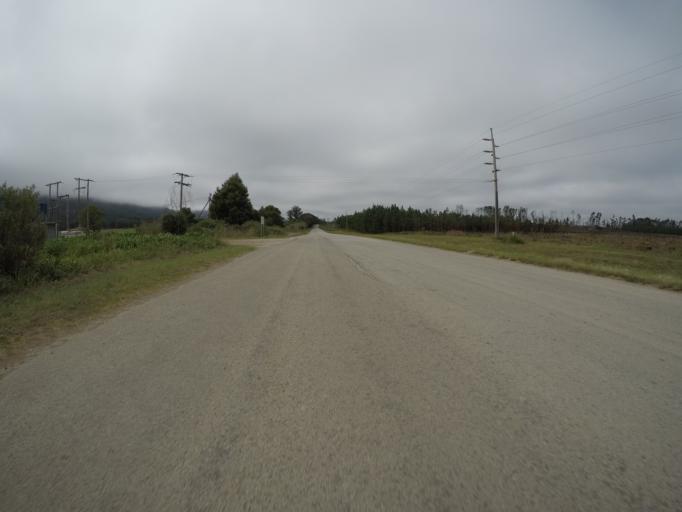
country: ZA
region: Eastern Cape
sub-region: Cacadu District Municipality
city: Kareedouw
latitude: -33.9965
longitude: 24.1415
